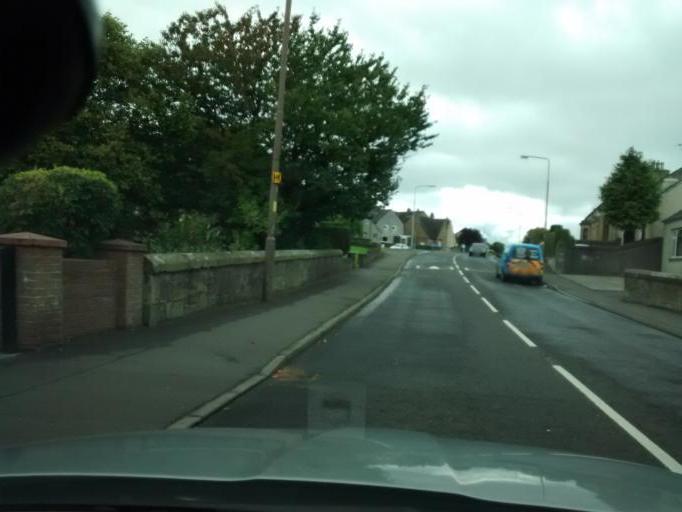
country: GB
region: Scotland
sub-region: West Lothian
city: Bathgate
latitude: 55.9049
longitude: -3.6491
